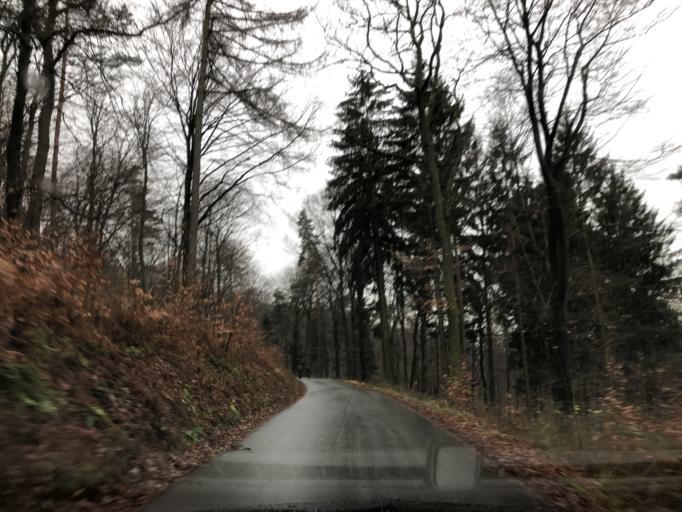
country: DE
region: Baden-Wuerttemberg
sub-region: Karlsruhe Region
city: Dossenheim
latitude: 49.4516
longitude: 8.7092
